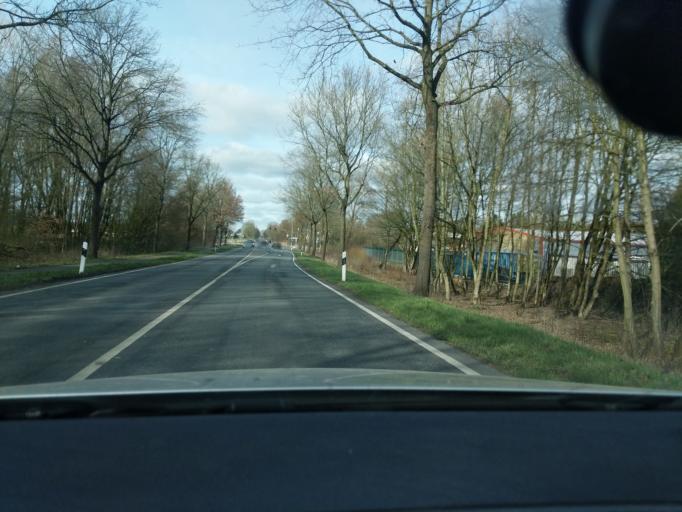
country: DE
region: Lower Saxony
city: Stade
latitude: 53.6181
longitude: 9.4966
